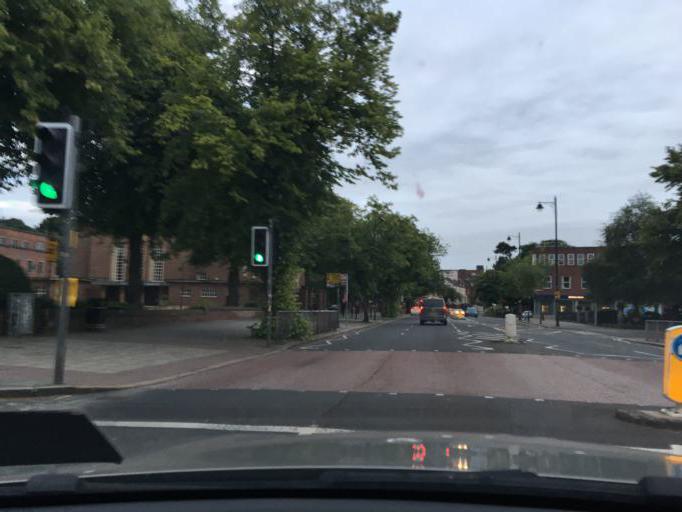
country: GB
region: Northern Ireland
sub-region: City of Belfast
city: Belfast
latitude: 54.5846
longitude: -5.9364
